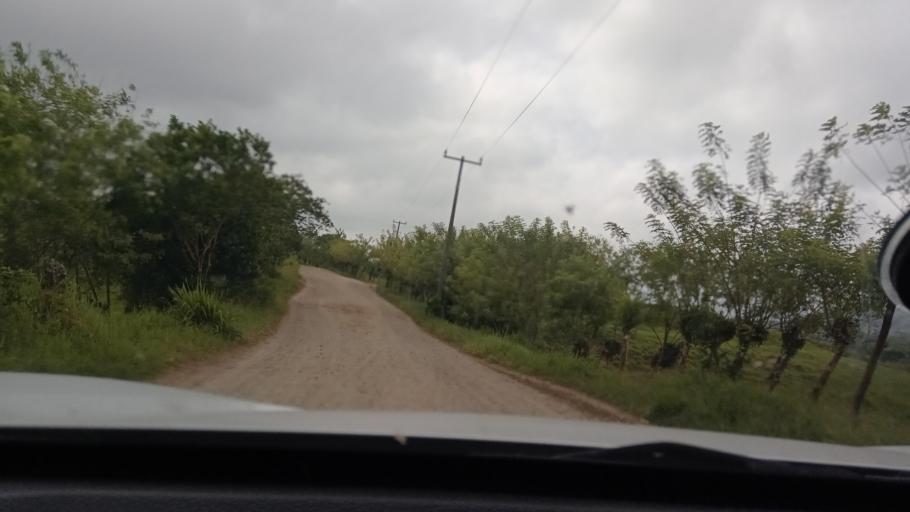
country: MX
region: Tabasco
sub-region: Huimanguillo
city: Francisco Rueda
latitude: 17.5662
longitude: -94.0266
